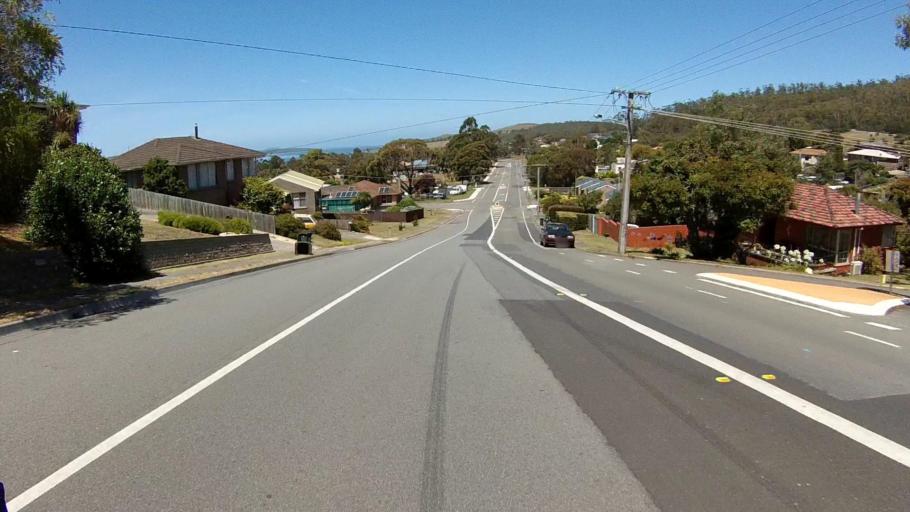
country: AU
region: Tasmania
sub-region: Clarence
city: Rokeby
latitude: -42.8930
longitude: 147.4314
